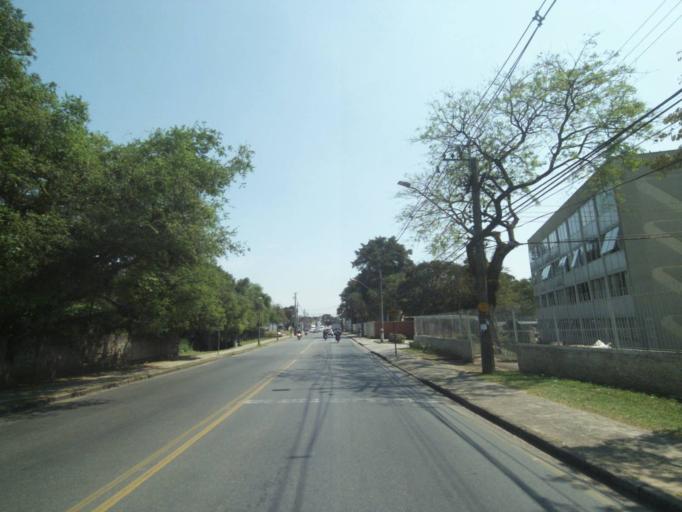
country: BR
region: Parana
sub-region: Curitiba
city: Curitiba
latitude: -25.4772
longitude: -49.3243
